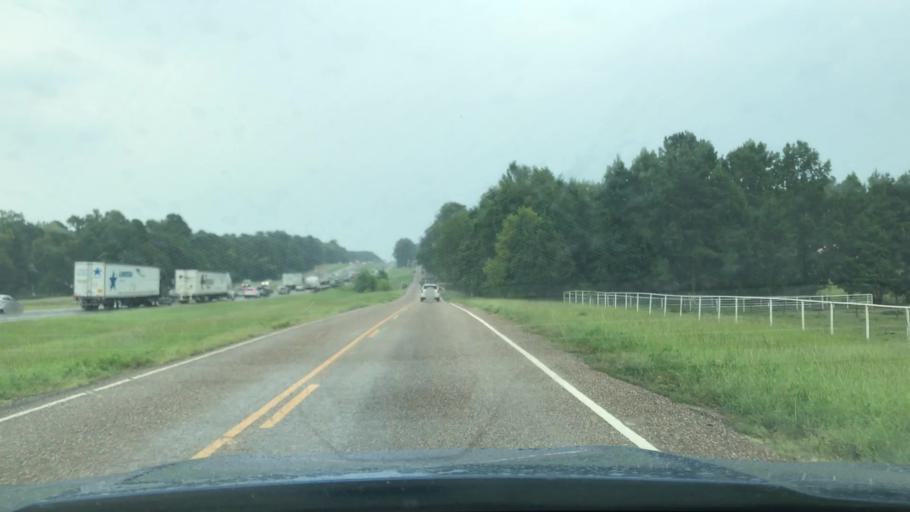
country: US
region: Texas
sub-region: Harrison County
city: Waskom
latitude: 32.4861
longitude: -94.1273
